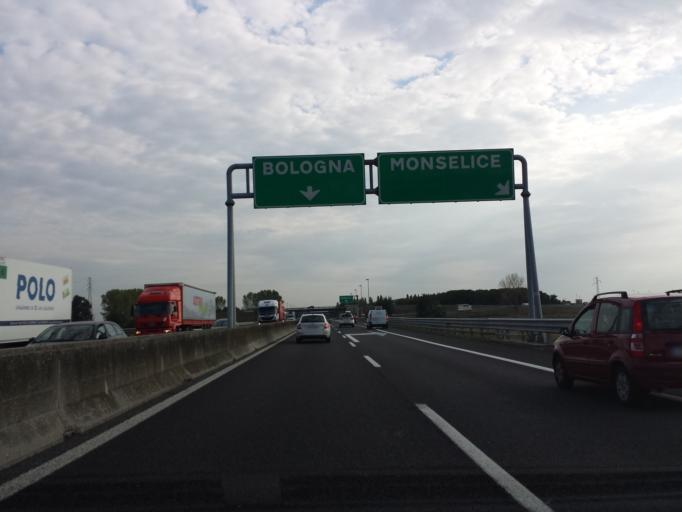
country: IT
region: Veneto
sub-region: Provincia di Padova
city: Pernumia
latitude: 45.2430
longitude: 11.7745
